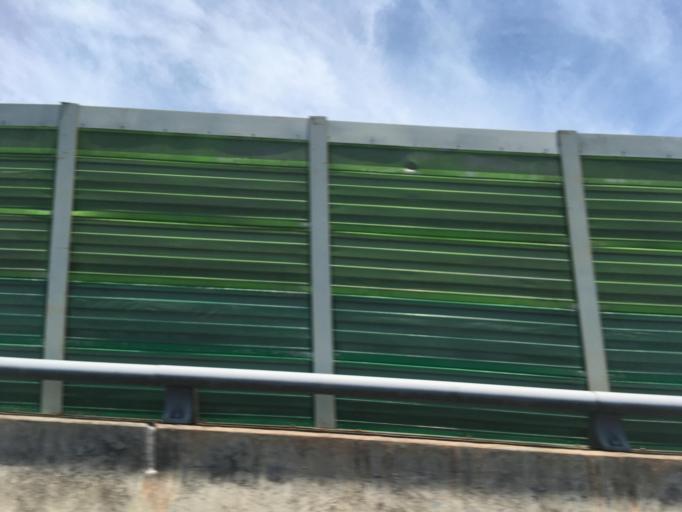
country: TW
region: Taipei
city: Taipei
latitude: 25.0355
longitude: 121.6239
